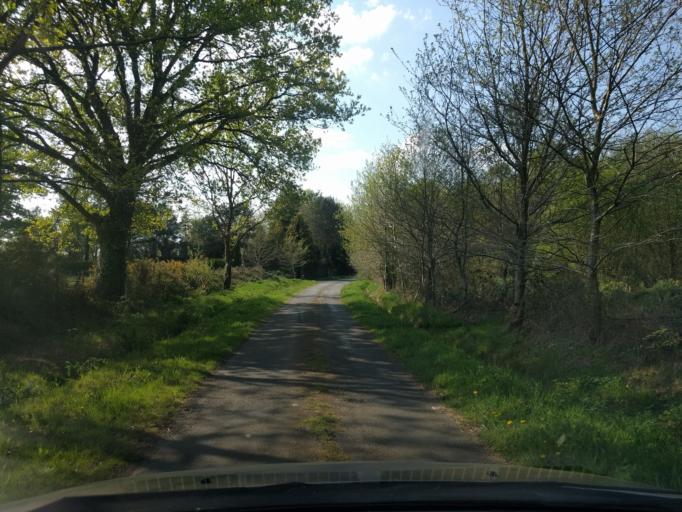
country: FR
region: Brittany
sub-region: Departement d'Ille-et-Vilaine
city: Gosne
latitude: 48.2873
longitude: -1.4508
